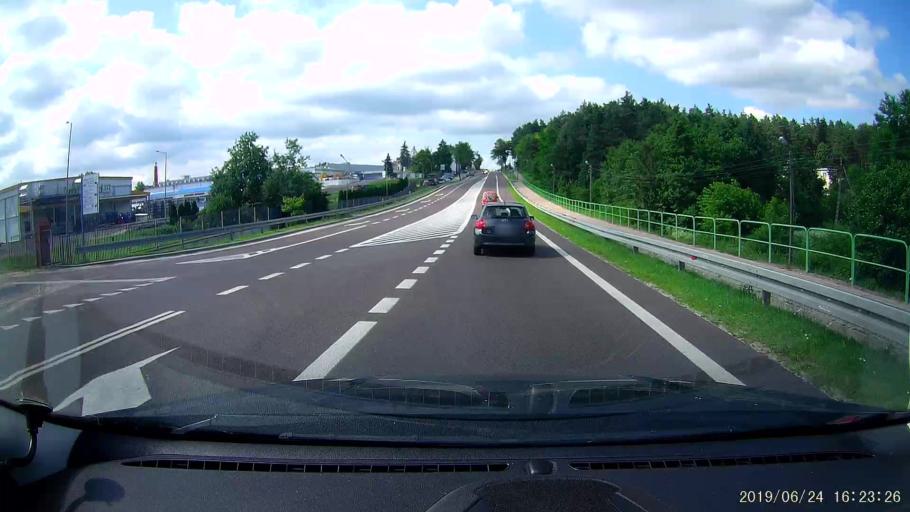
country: PL
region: Lublin Voivodeship
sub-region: Powiat tomaszowski
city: Tomaszow Lubelski
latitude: 50.4316
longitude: 23.4216
